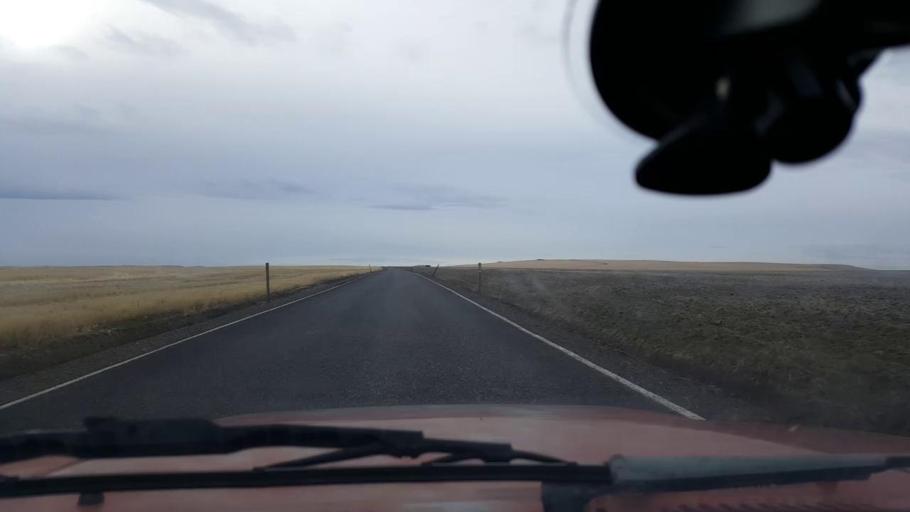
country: US
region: Washington
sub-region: Asotin County
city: Clarkston Heights-Vineland
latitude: 46.3545
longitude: -117.2256
